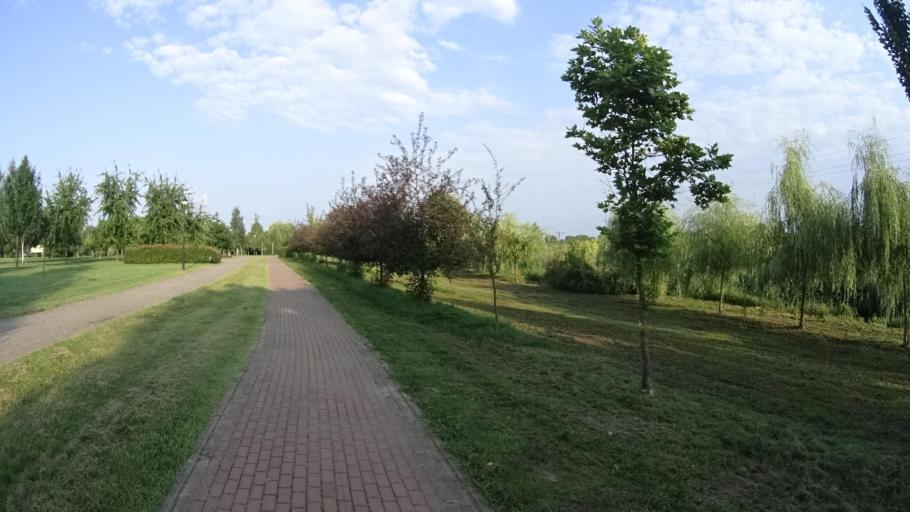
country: PL
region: Masovian Voivodeship
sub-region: Powiat pruszkowski
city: Raszyn
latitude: 52.1479
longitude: 20.9259
